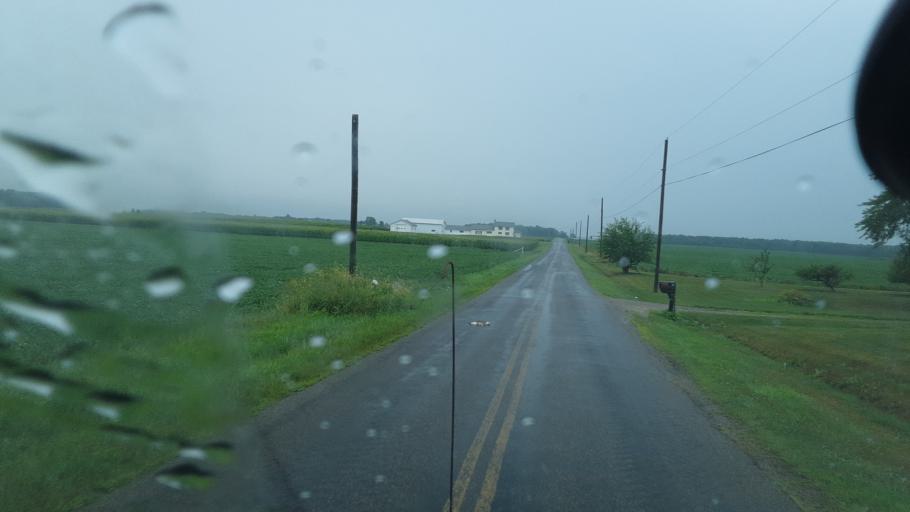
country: US
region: Ohio
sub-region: Williams County
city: Edgerton
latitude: 41.5179
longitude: -84.7881
